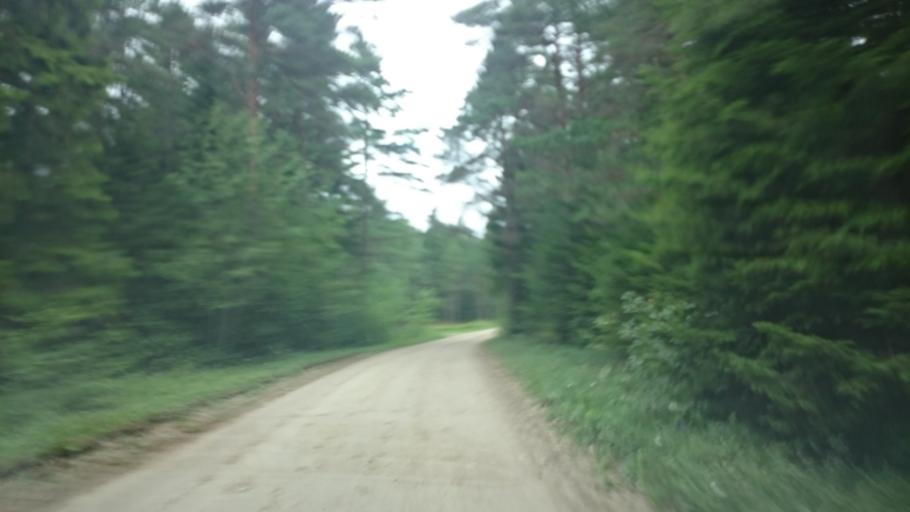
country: EE
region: Saare
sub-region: Orissaare vald
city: Orissaare
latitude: 58.5907
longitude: 22.7046
